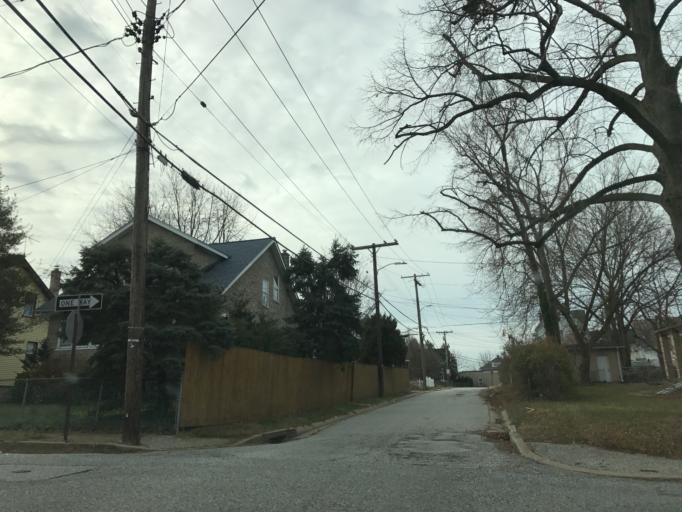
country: US
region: Maryland
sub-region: Baltimore County
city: Overlea
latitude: 39.3474
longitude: -76.5352
